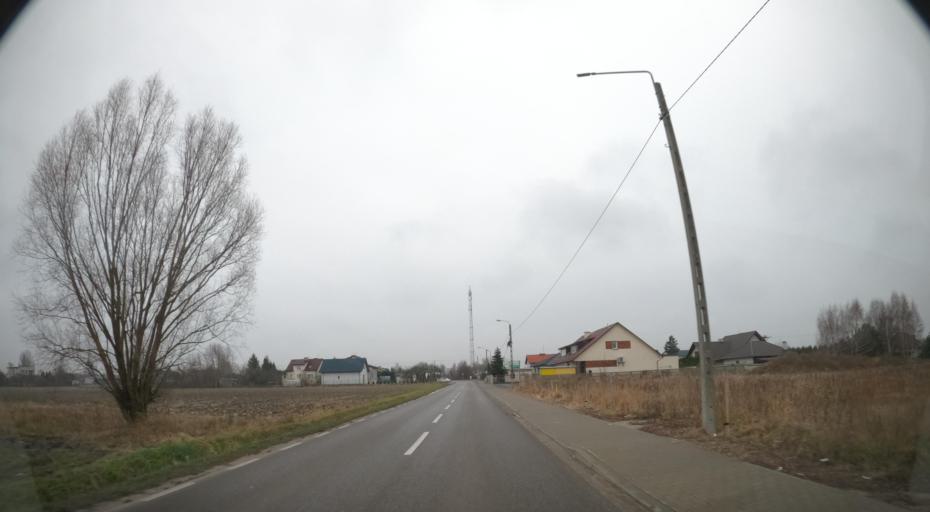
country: PL
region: Masovian Voivodeship
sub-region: Powiat radomski
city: Skaryszew
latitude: 51.3790
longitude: 21.2534
